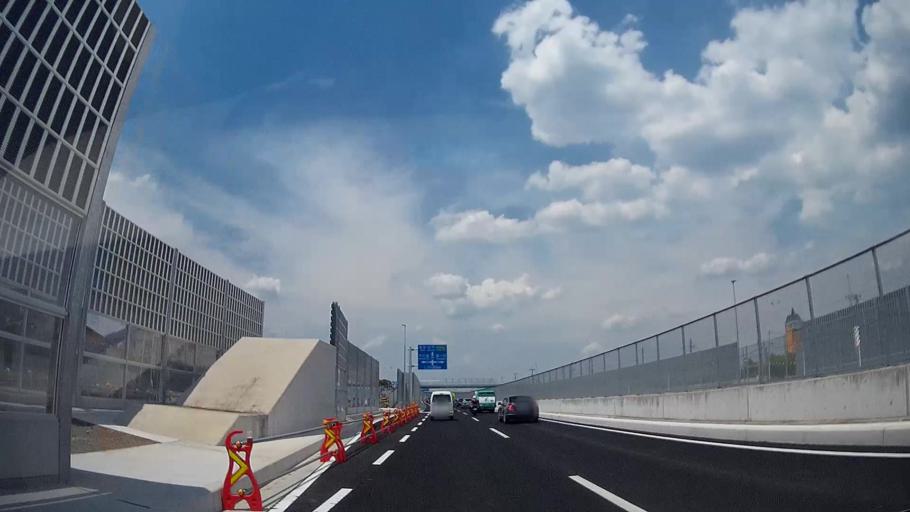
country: JP
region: Chiba
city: Matsudo
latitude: 35.7402
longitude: 139.9203
